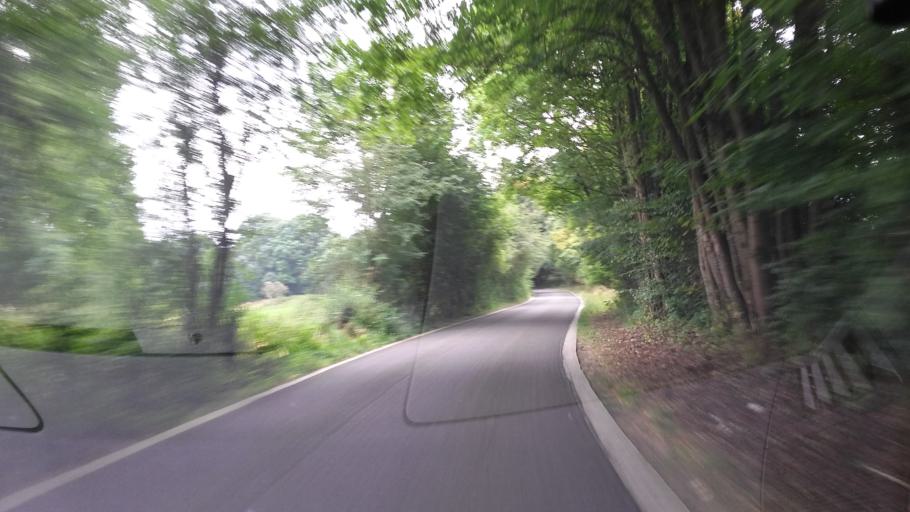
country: BE
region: Wallonia
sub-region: Province du Luxembourg
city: Arlon
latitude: 49.6683
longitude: 5.8353
